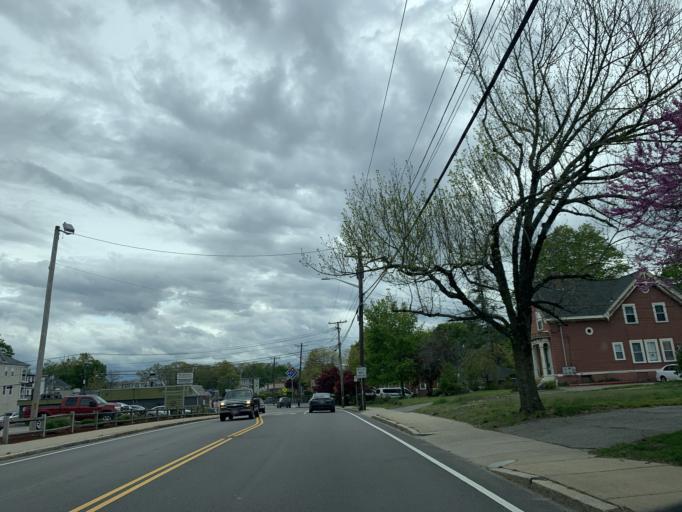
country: US
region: Massachusetts
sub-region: Bristol County
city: Attleboro
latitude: 41.9355
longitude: -71.2979
